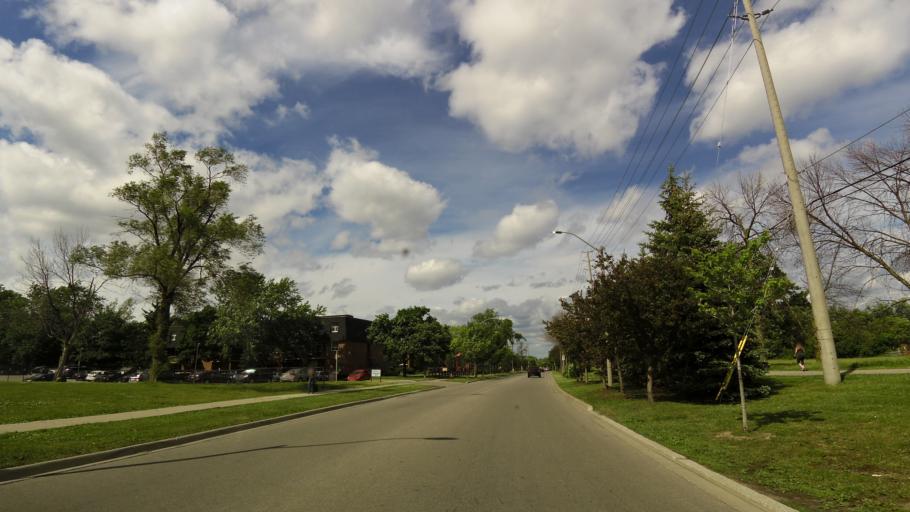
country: CA
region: Ontario
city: Mississauga
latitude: 43.5276
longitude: -79.6603
